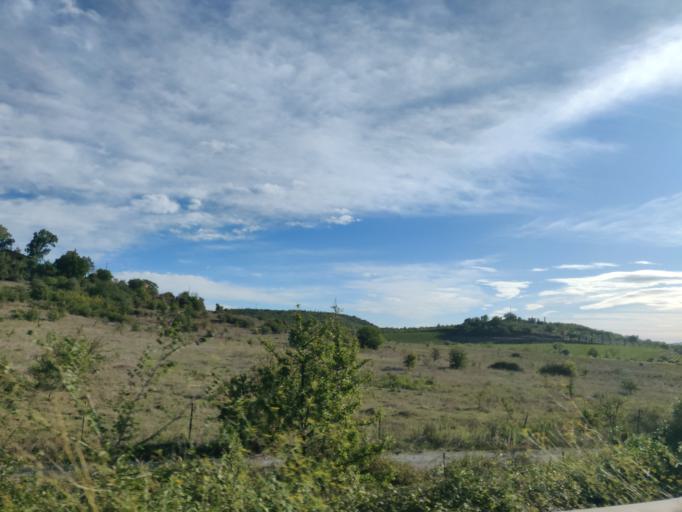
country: IT
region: Tuscany
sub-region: Provincia di Grosseto
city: Gavorrano
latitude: 42.9215
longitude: 10.9576
